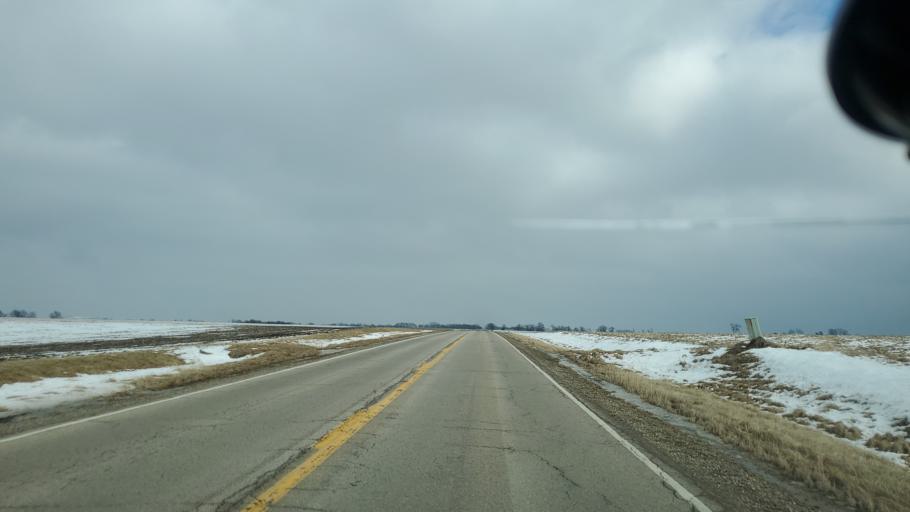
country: US
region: Illinois
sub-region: Marshall County
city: Toluca
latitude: 41.1186
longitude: -89.1852
